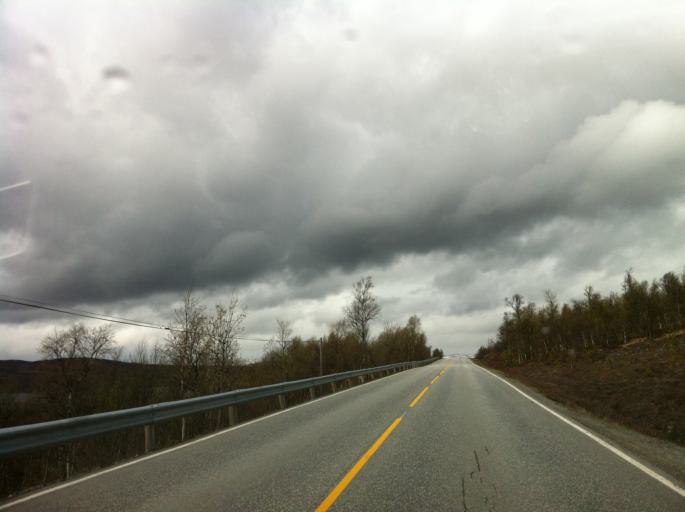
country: NO
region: Sor-Trondelag
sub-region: Roros
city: Roros
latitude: 62.5963
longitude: 11.8258
